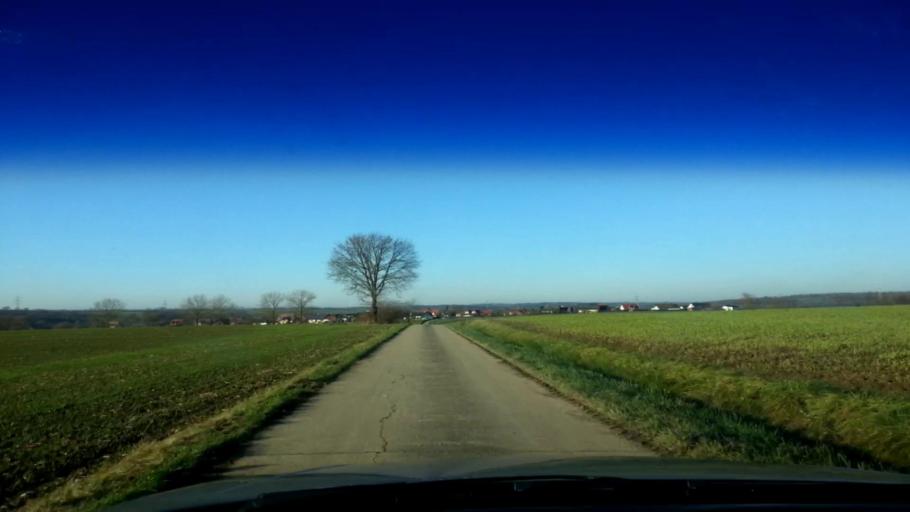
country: DE
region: Bavaria
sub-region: Upper Franconia
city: Schesslitz
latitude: 49.9528
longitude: 11.0059
